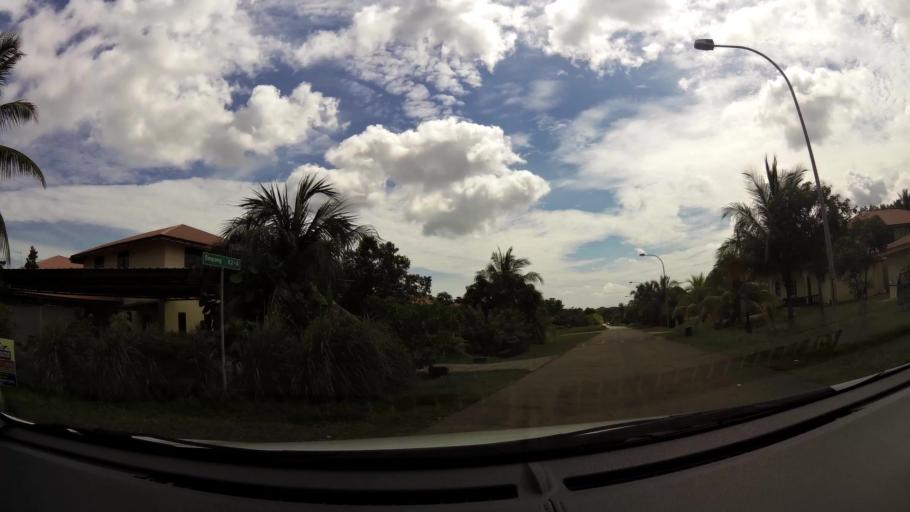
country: BN
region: Brunei and Muara
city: Bandar Seri Begawan
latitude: 4.9379
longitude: 114.9004
